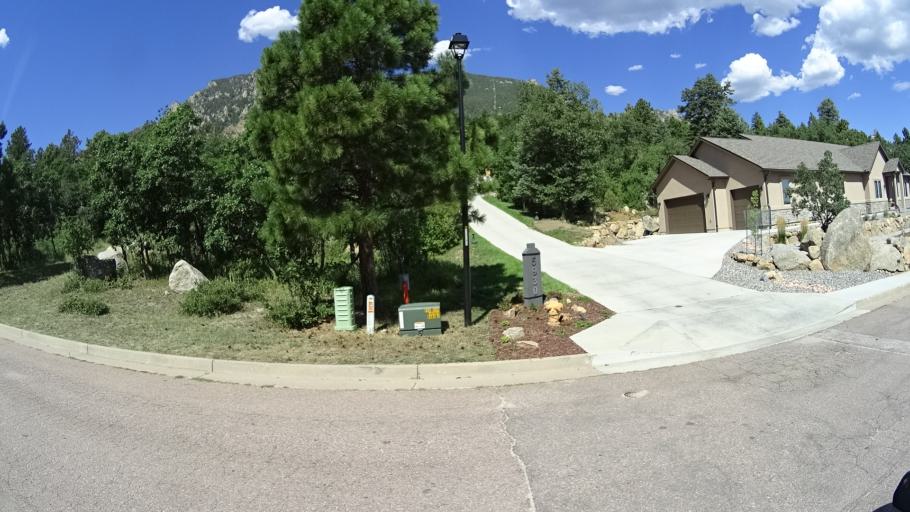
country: US
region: Colorado
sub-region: El Paso County
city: Fort Carson
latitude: 38.7437
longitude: -104.8365
